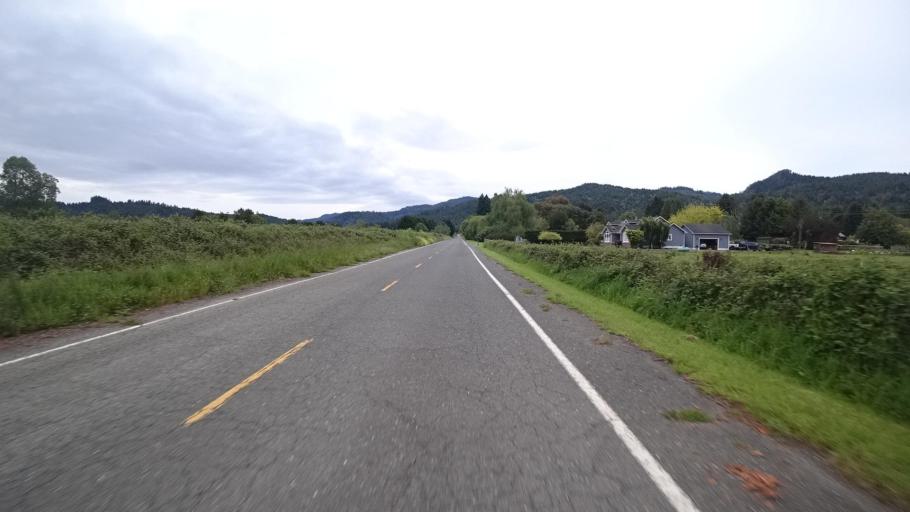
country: US
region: California
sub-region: Humboldt County
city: Blue Lake
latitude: 40.8670
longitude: -123.9957
